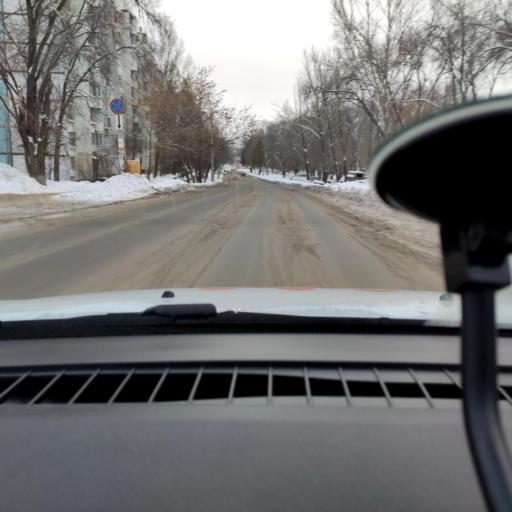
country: RU
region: Samara
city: Samara
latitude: 53.2053
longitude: 50.2210
